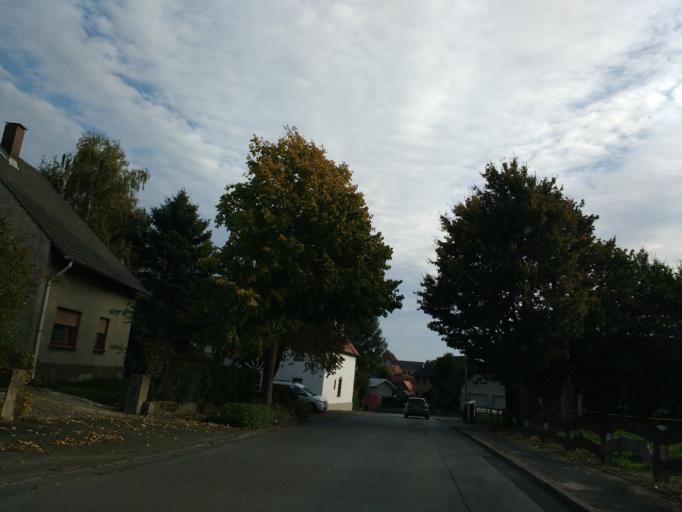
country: DE
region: North Rhine-Westphalia
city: Lichtenau
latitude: 51.6747
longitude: 8.8323
